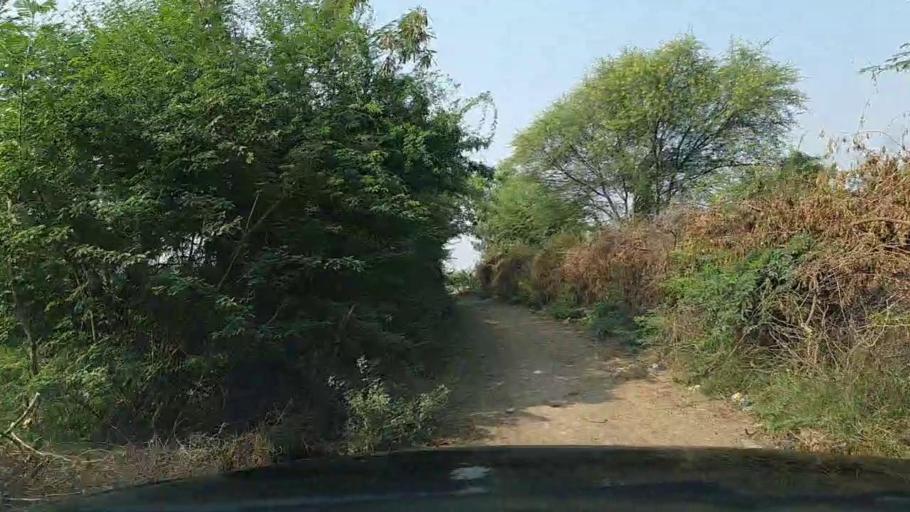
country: PK
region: Sindh
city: Mirpur Batoro
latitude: 24.6830
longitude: 68.2368
